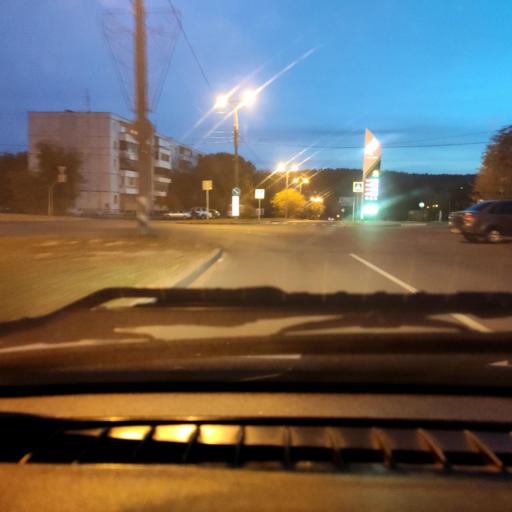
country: RU
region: Samara
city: Zhigulevsk
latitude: 53.4700
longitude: 49.5379
